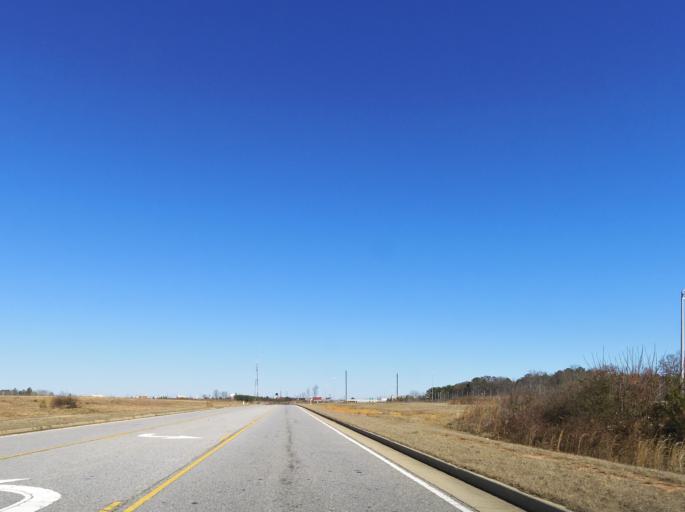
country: US
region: Georgia
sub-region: Peach County
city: Byron
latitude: 32.7328
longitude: -83.7250
